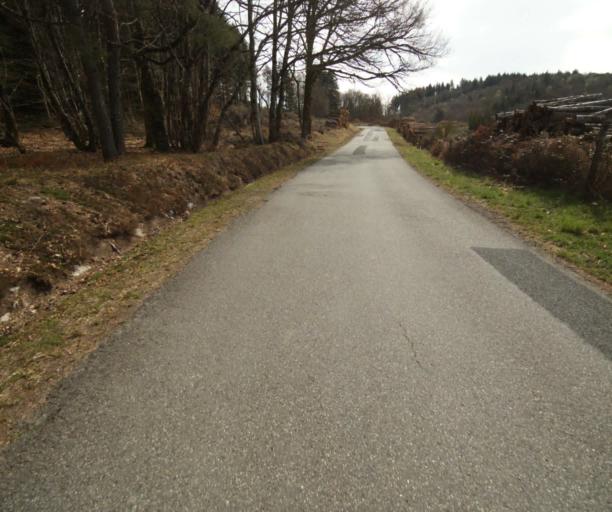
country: FR
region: Limousin
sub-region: Departement de la Correze
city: Correze
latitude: 45.3706
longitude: 1.9132
